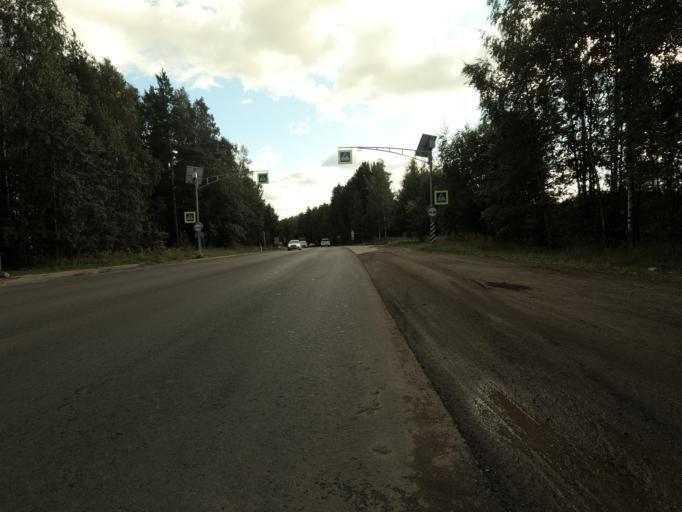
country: RU
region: Leningrad
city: Koltushi
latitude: 59.9544
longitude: 30.6570
